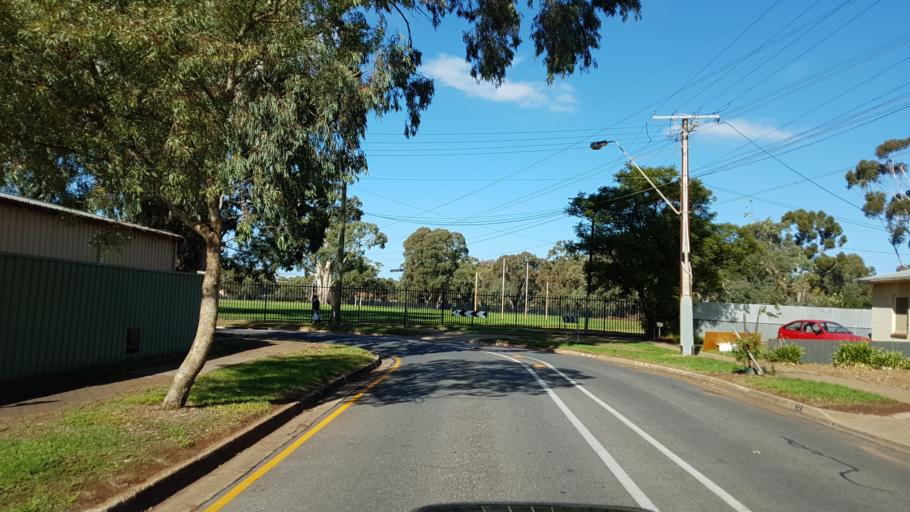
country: AU
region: South Australia
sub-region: Salisbury
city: Salisbury
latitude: -34.7563
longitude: 138.6385
